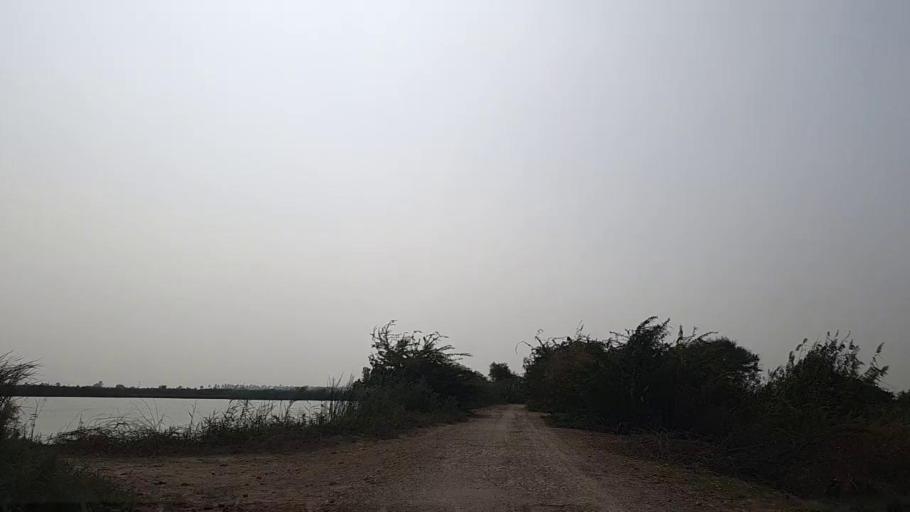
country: PK
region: Sindh
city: Thatta
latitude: 24.6977
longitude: 67.8009
